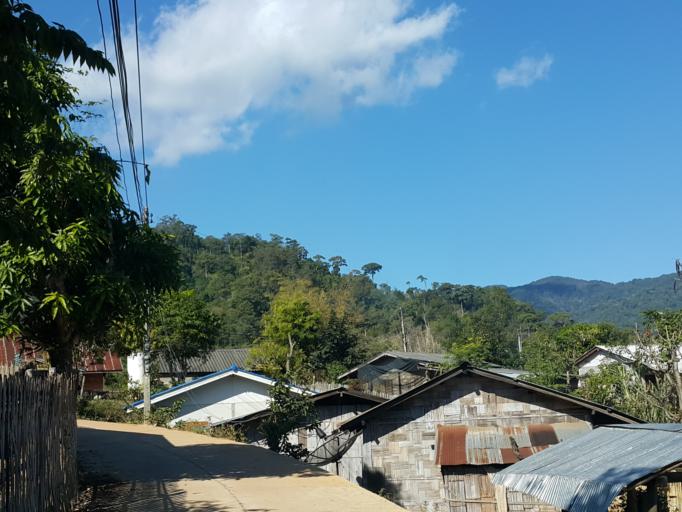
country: TH
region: Chiang Mai
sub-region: Amphoe Chiang Dao
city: Chiang Dao
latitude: 19.5256
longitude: 98.8611
